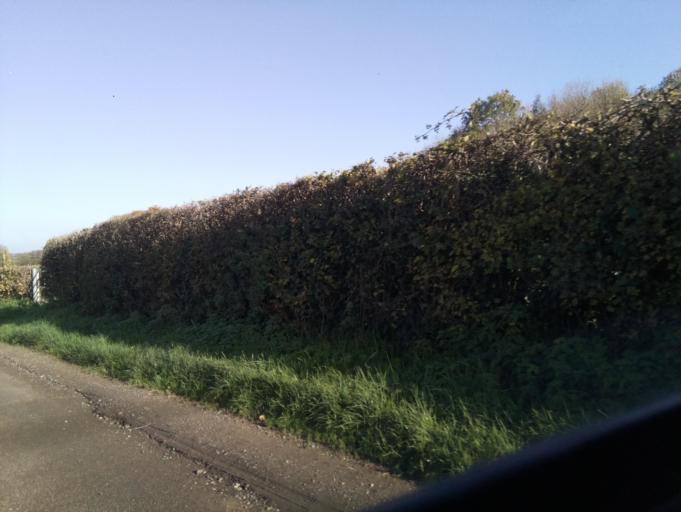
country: GB
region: England
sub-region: Somerset
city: Castle Cary
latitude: 51.0740
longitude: -2.4741
